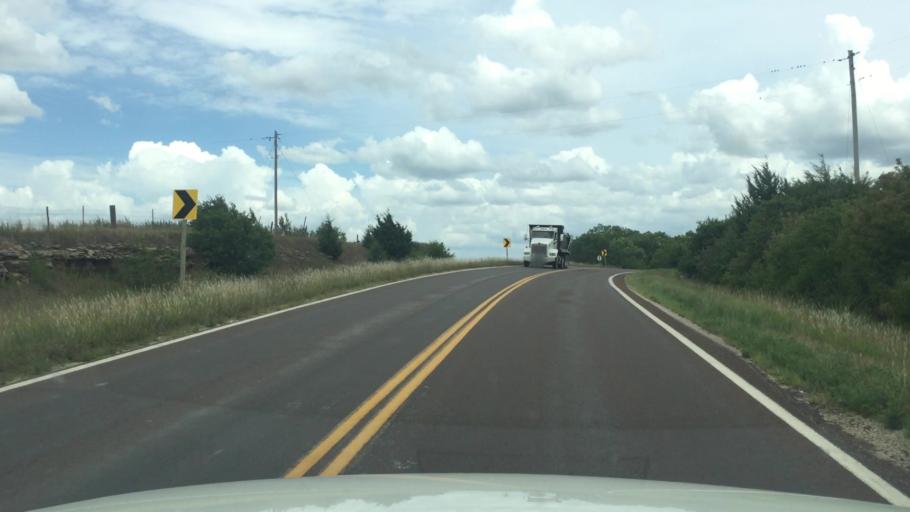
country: US
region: Kansas
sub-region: Shawnee County
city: Topeka
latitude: 39.0294
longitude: -95.5058
